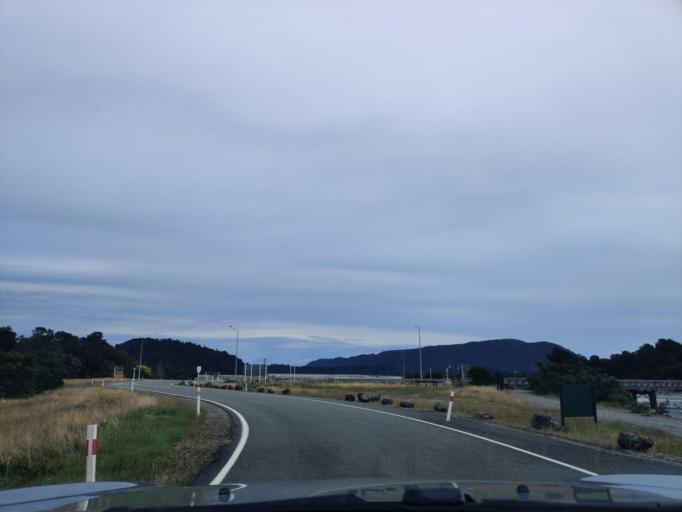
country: NZ
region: West Coast
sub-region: Westland District
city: Hokitika
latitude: -43.3945
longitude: 170.1804
